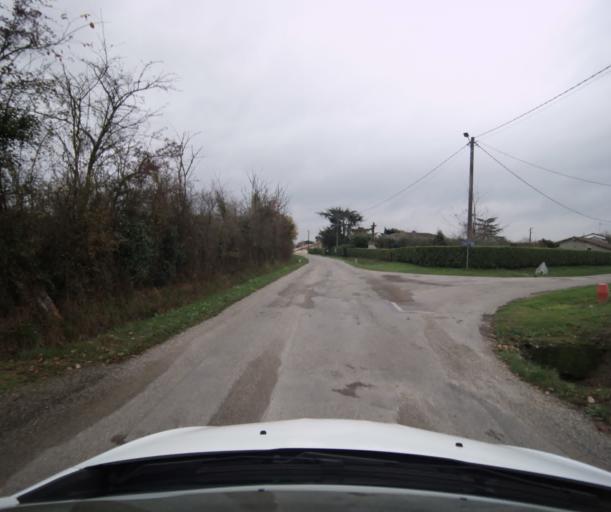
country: FR
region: Midi-Pyrenees
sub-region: Departement du Tarn-et-Garonne
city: Moissac
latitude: 44.0740
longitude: 1.1358
